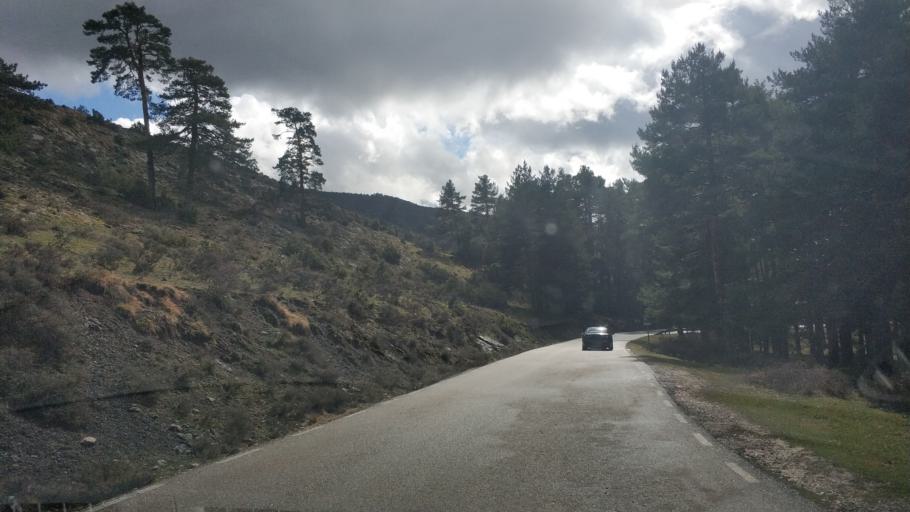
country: ES
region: Castille and Leon
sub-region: Provincia de Burgos
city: Neila
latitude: 42.0394
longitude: -3.0044
